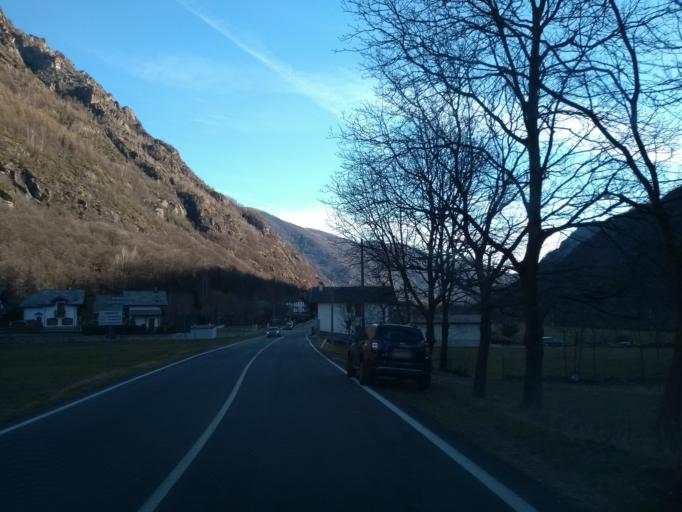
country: IT
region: Piedmont
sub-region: Provincia di Torino
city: Chialamberto
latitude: 45.3576
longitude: 7.3566
